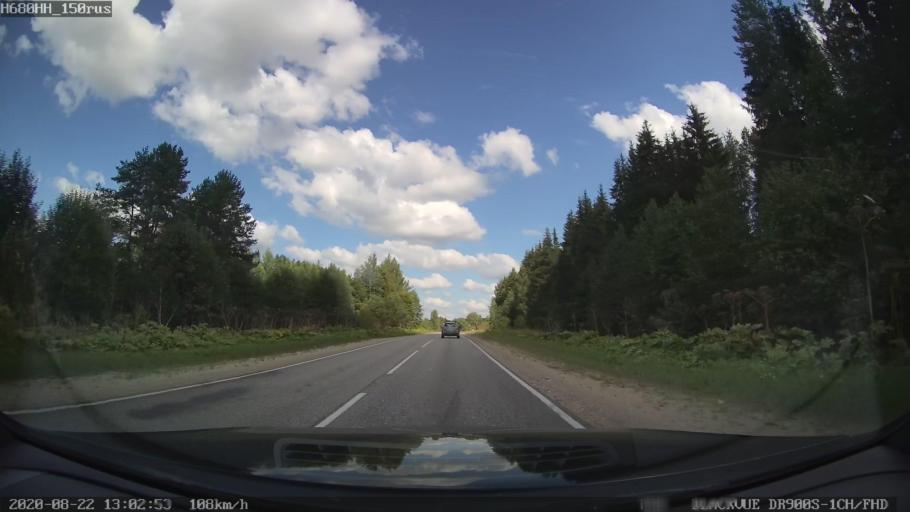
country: RU
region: Tverskaya
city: Bezhetsk
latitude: 57.6548
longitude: 36.4033
